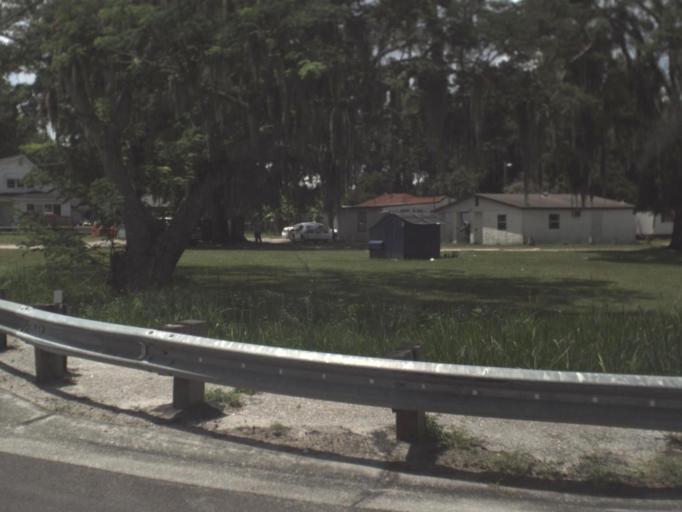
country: US
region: Florida
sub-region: Hillsborough County
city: Dover
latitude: 27.9985
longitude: -82.2033
